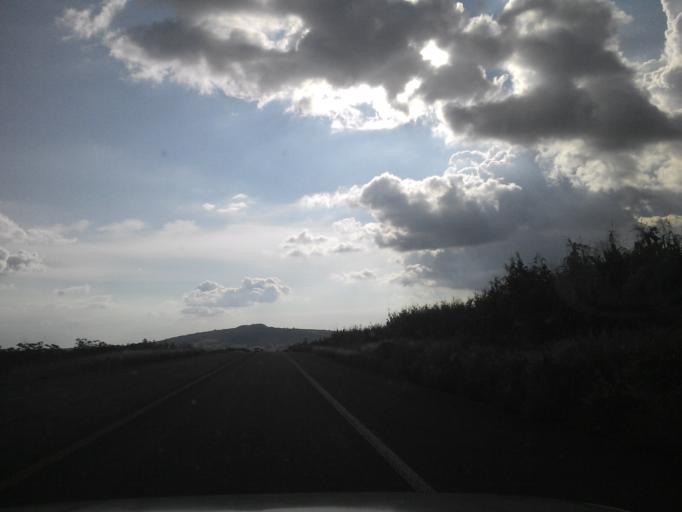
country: MX
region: Jalisco
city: Atotonilco el Alto
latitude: 20.5779
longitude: -102.5060
